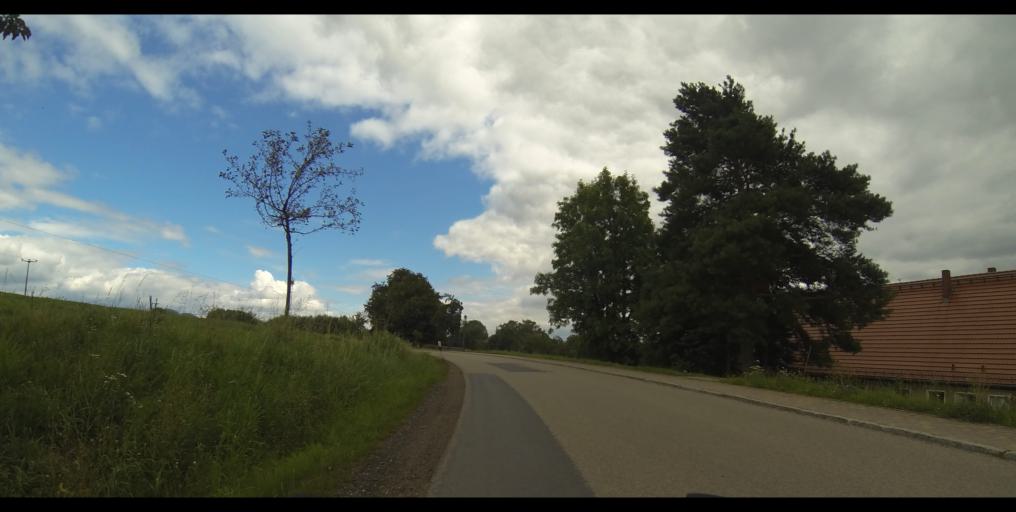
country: DE
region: Saxony
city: Wilsdruff
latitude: 51.0519
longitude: 13.5659
